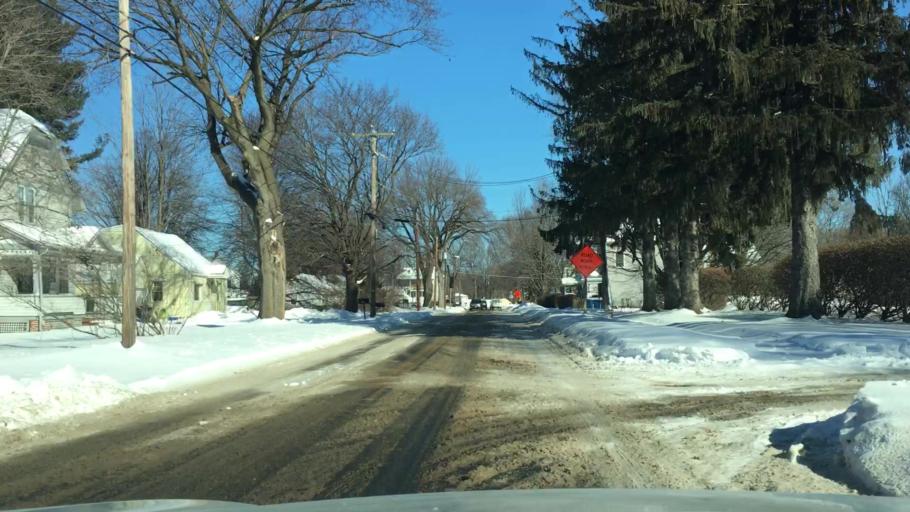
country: US
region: Massachusetts
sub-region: Hampden County
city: Chicopee
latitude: 42.1416
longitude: -72.6221
